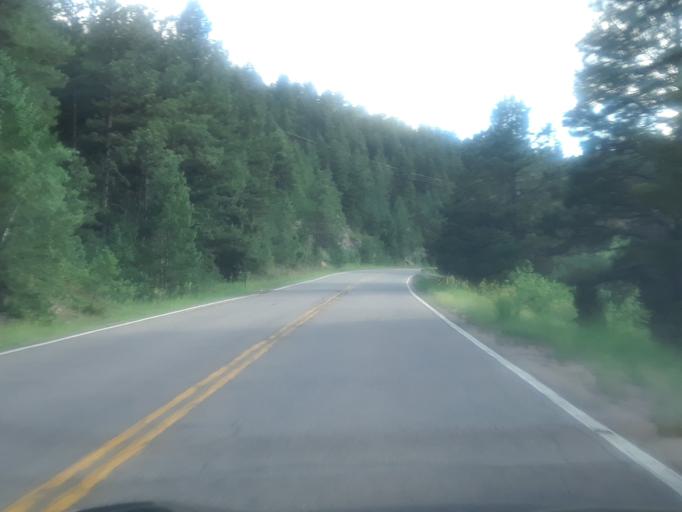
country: US
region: Colorado
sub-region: Jefferson County
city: Kittredge
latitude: 39.7177
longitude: -105.3595
